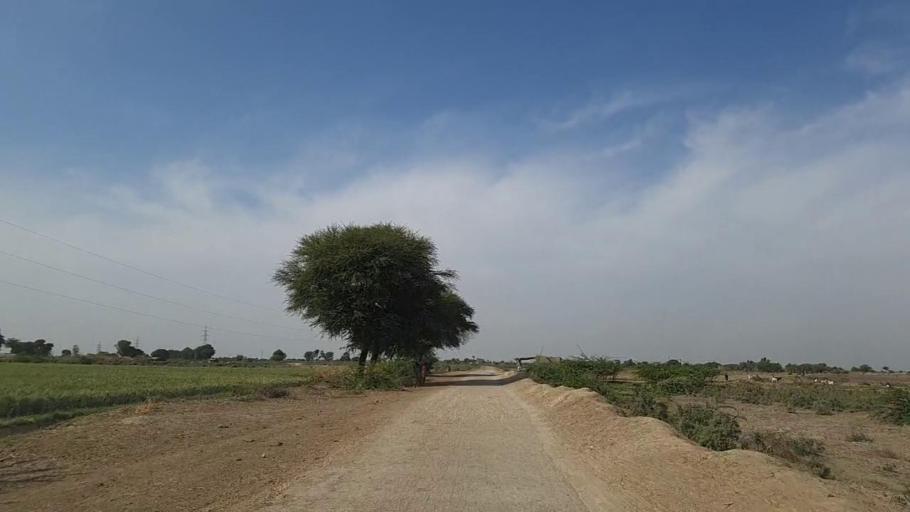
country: PK
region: Sindh
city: Samaro
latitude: 25.2209
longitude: 69.4503
